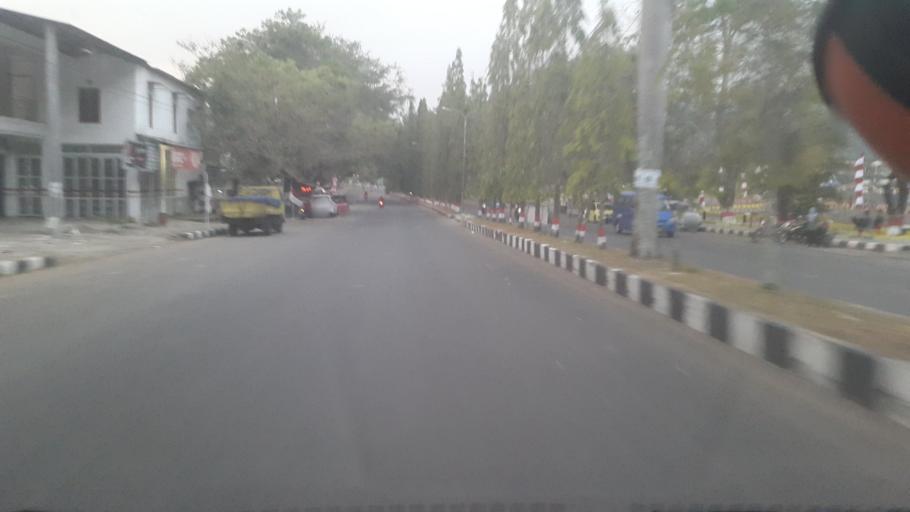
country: ID
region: West Java
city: Pelabuhanratu
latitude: -6.9935
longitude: 106.5576
